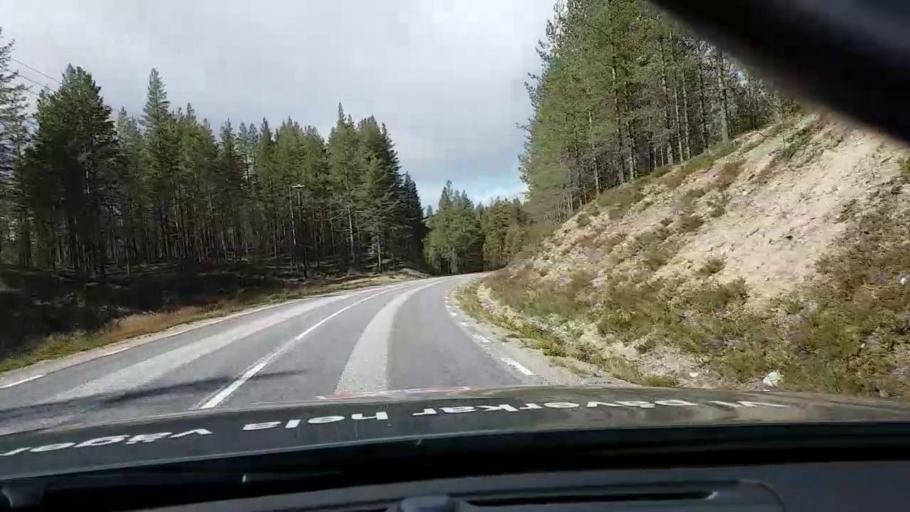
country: SE
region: Vaesterbotten
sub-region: Asele Kommun
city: Asele
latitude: 63.8567
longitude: 17.3854
